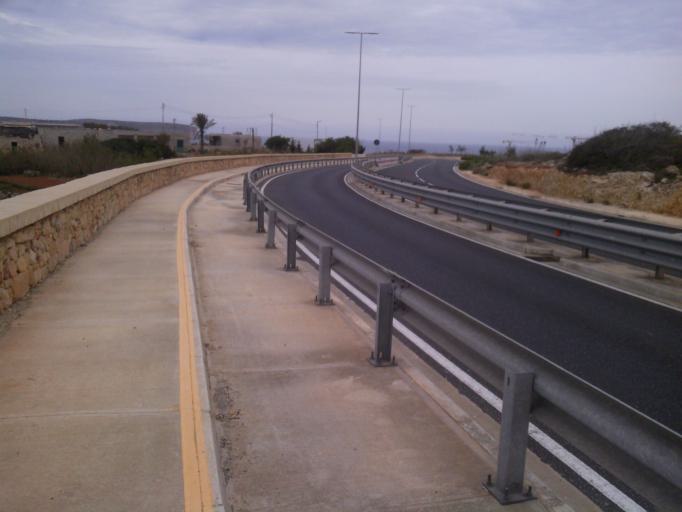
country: MT
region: Il-Mellieha
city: Mellieha
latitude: 35.9824
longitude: 14.3410
